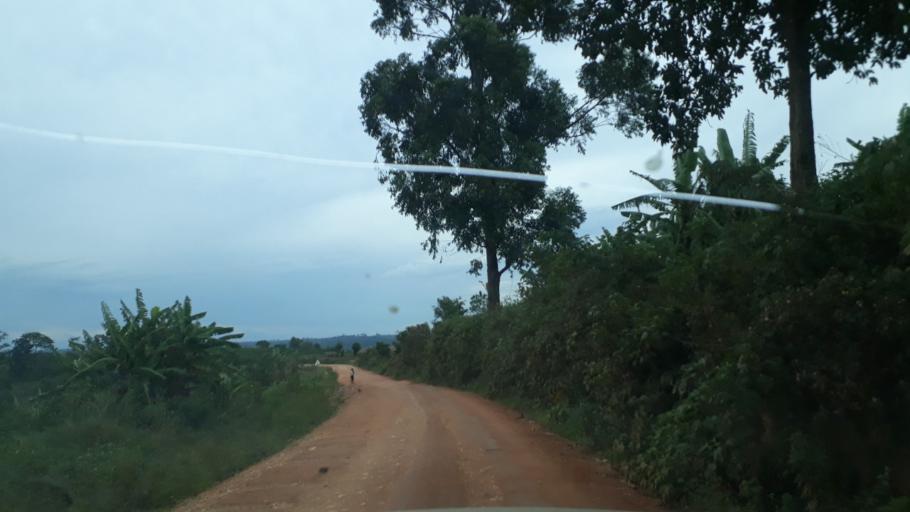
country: UG
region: Northern Region
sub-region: Zombo District
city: Paidha
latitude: 2.0608
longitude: 30.6350
